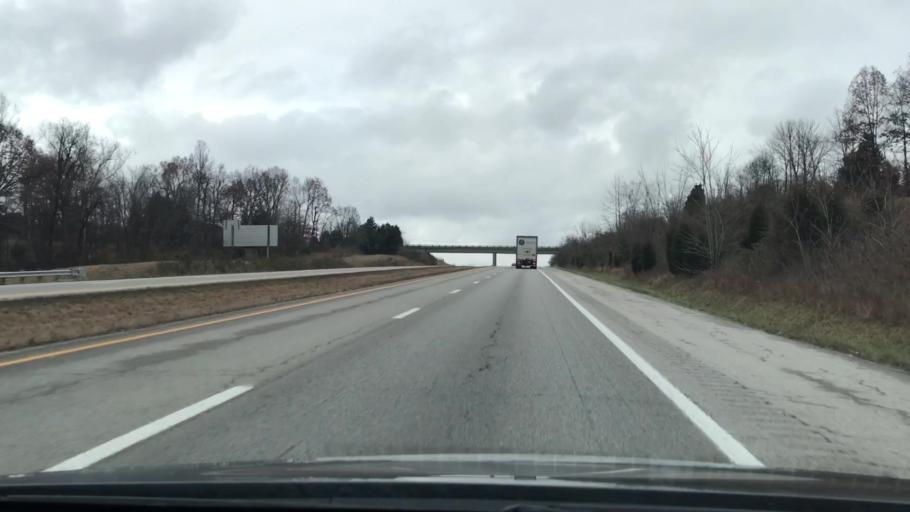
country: US
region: Kentucky
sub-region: Christian County
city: Hopkinsville
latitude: 36.9212
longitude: -87.4731
